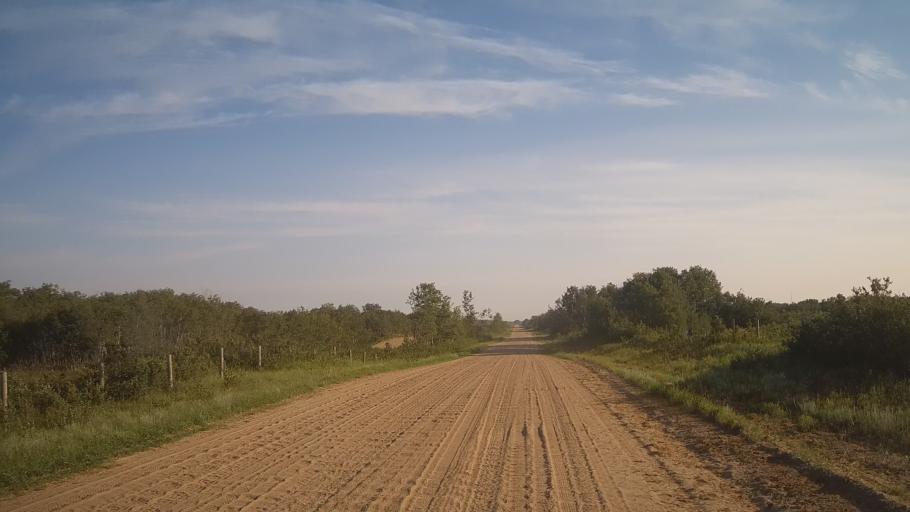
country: CA
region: Saskatchewan
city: Saskatoon
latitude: 51.8451
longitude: -106.5238
